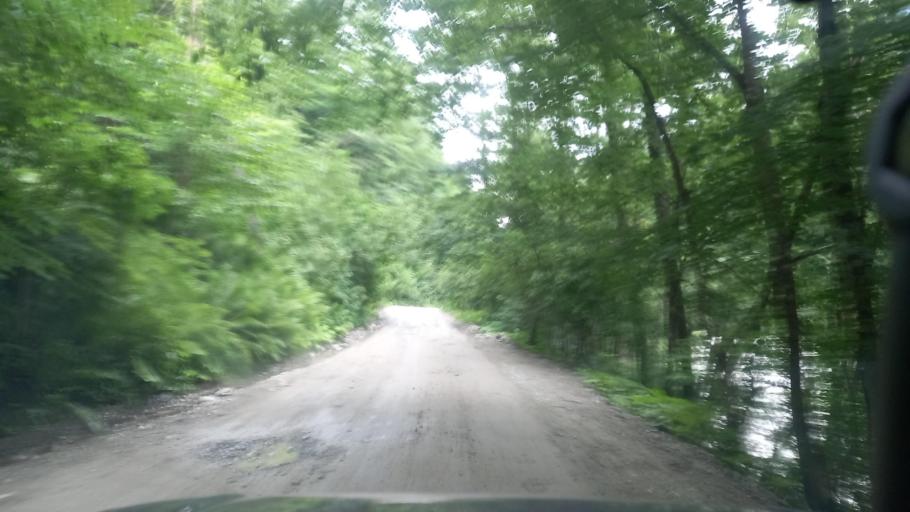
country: RU
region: Karachayevo-Cherkesiya
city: Kurdzhinovo
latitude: 43.8718
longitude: 40.9489
